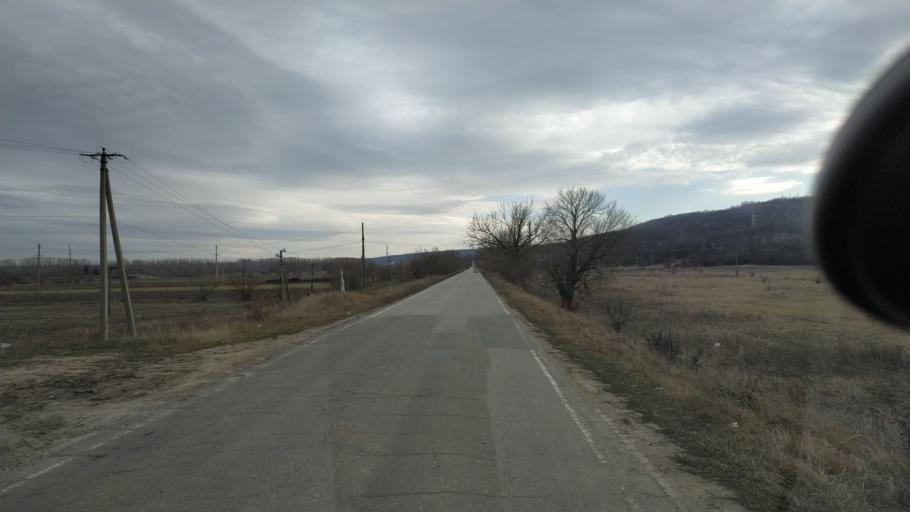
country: MD
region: Chisinau
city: Vadul lui Voda
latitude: 47.1150
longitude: 29.0576
